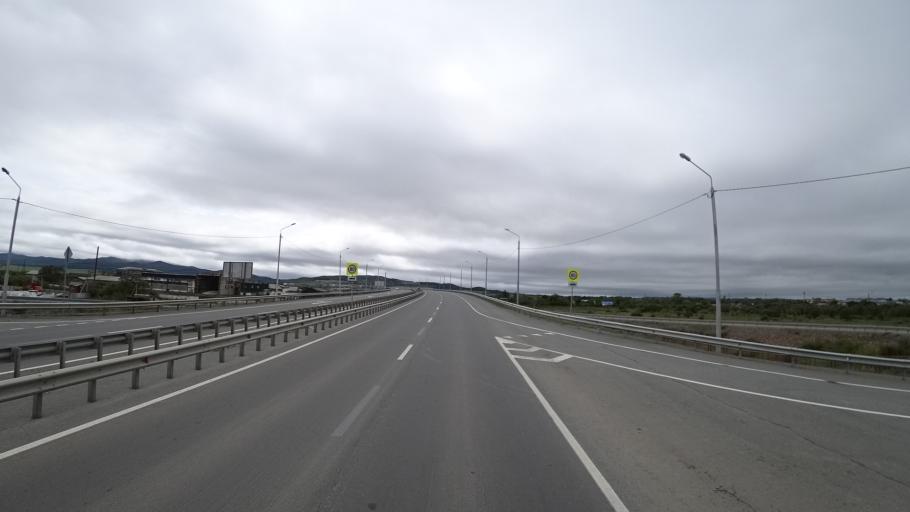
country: RU
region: Primorskiy
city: Monastyrishche
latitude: 44.1951
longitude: 132.4438
